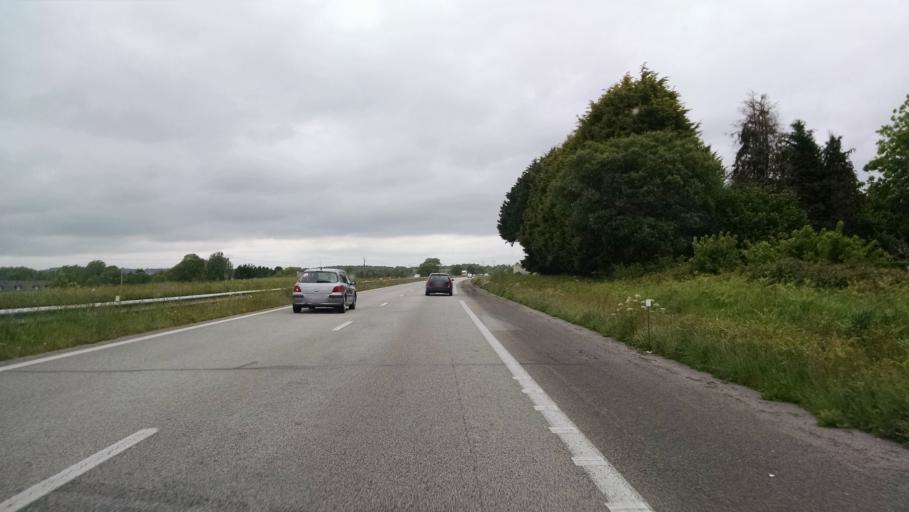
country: FR
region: Brittany
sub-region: Departement du Finistere
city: Landrevarzec
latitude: 48.0824
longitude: -4.0434
